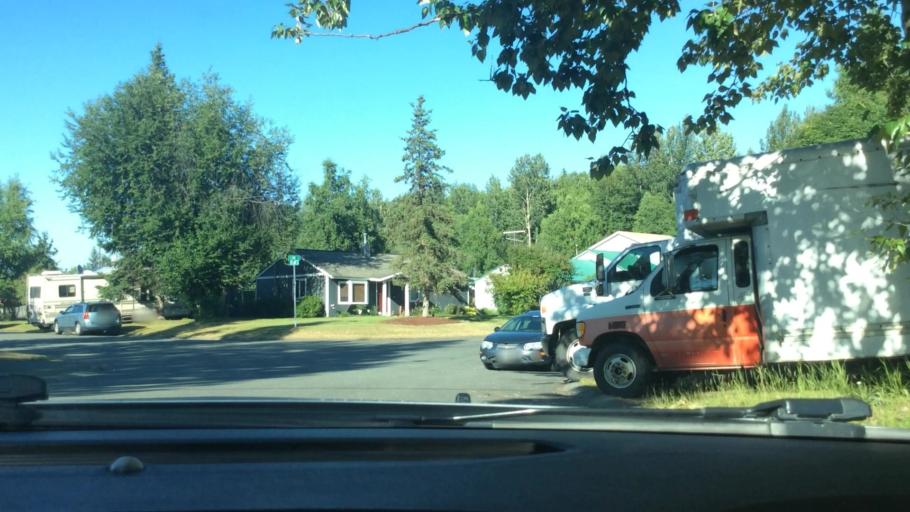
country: US
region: Alaska
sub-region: Anchorage Municipality
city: Anchorage
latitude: 61.2048
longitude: -149.7687
